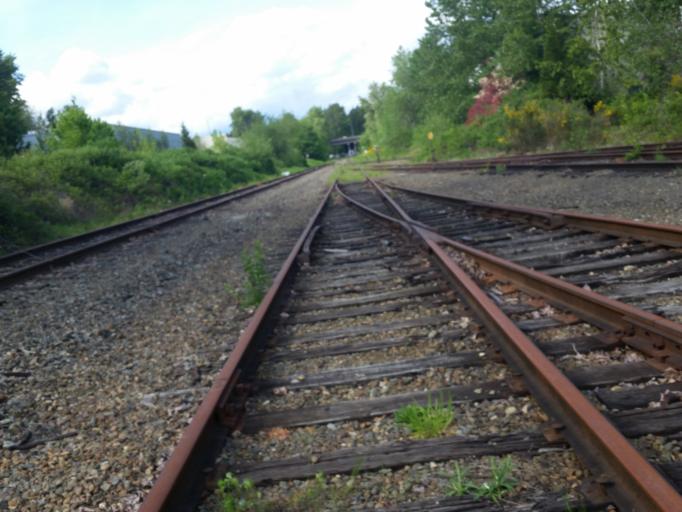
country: US
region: Washington
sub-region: King County
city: Bellevue
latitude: 47.6279
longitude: -122.1835
